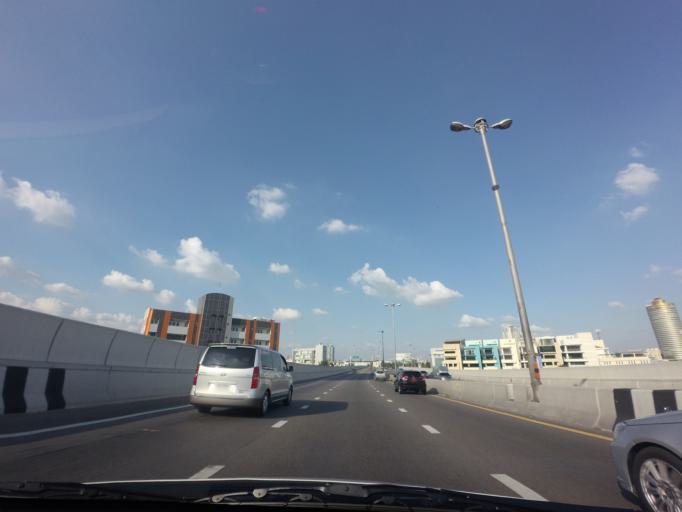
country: TH
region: Bangkok
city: Yan Nawa
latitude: 13.6800
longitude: 100.5400
